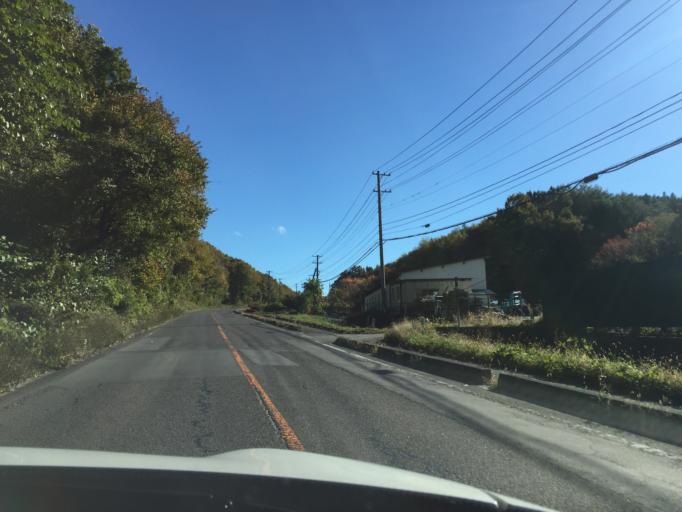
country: JP
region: Fukushima
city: Funehikimachi-funehiki
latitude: 37.2570
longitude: 140.6379
